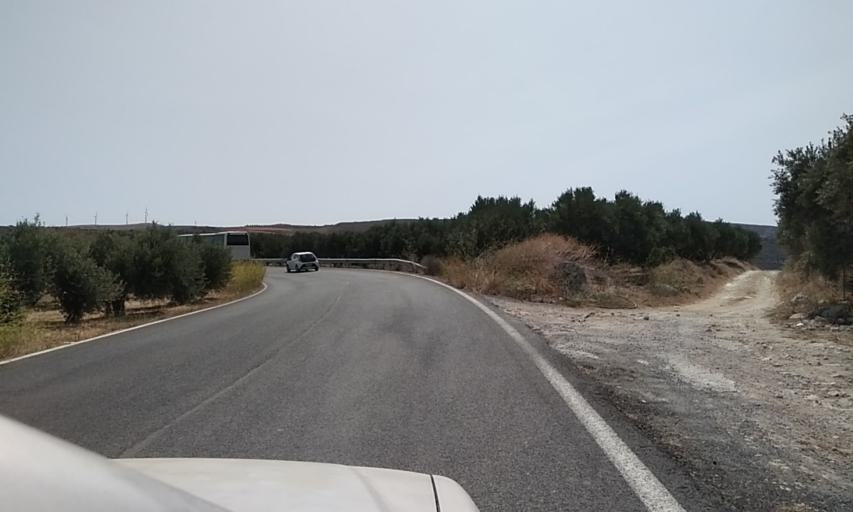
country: GR
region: Crete
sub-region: Nomos Lasithiou
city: Makry-Gialos
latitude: 35.0987
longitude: 26.0595
